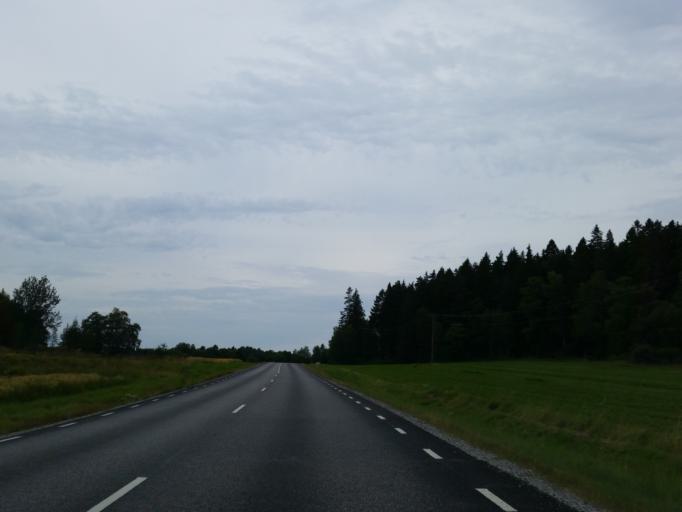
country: SE
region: Stockholm
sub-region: Salems Kommun
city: Ronninge
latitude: 59.2275
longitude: 17.7271
